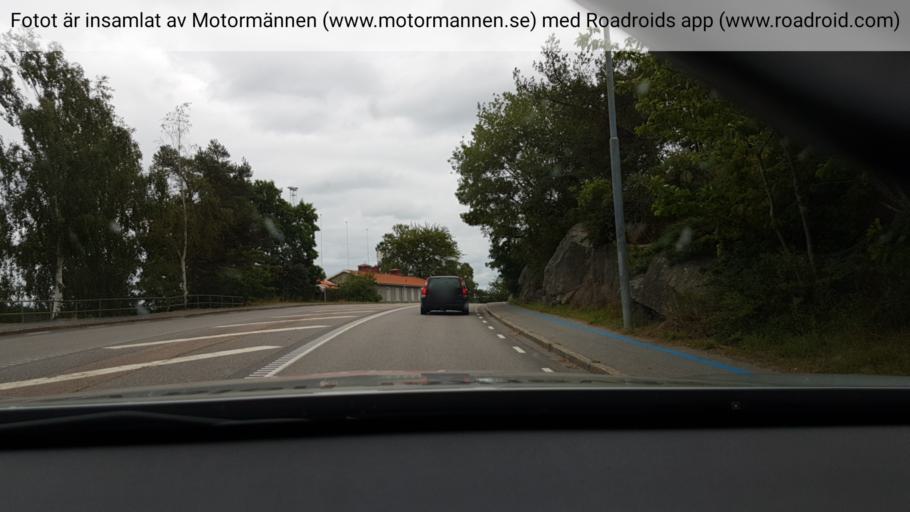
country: SE
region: Stockholm
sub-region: Nynashamns Kommun
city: Nynashamn
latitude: 58.9072
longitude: 17.9542
